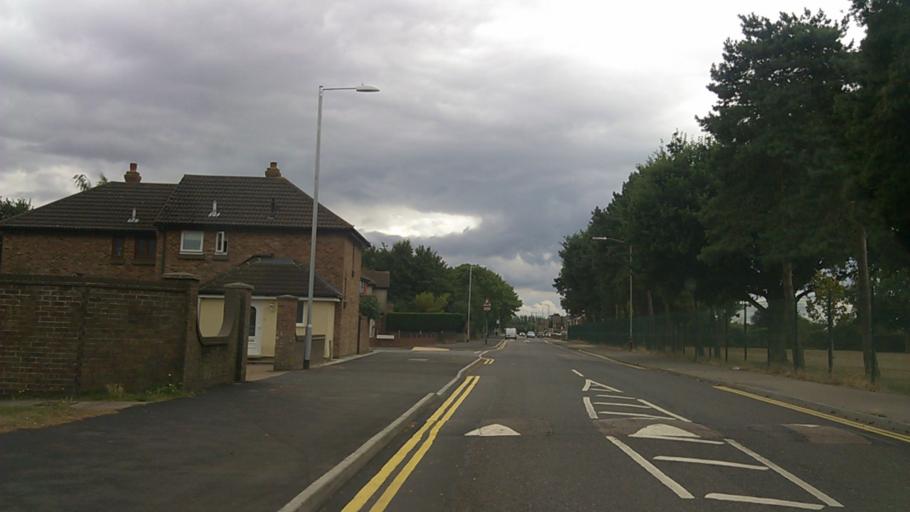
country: GB
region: England
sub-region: Essex
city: Eight Ash Green
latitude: 51.8820
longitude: 0.8415
